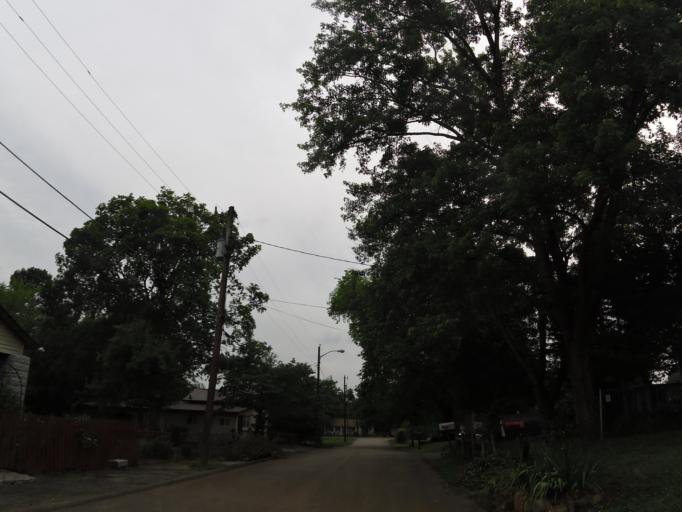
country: US
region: Tennessee
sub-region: Knox County
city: Knoxville
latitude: 35.9536
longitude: -83.9577
